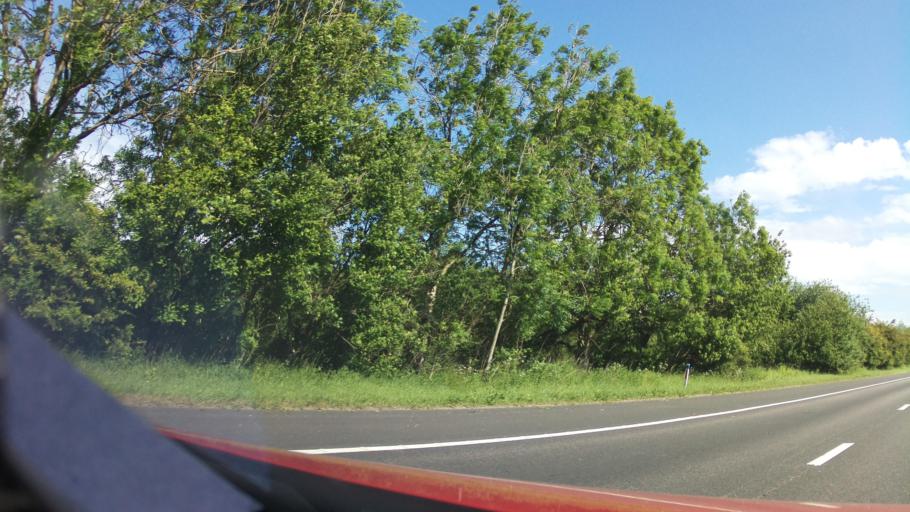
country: GB
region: England
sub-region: Borough of Bolton
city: Horwich
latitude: 53.5879
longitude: -2.5589
